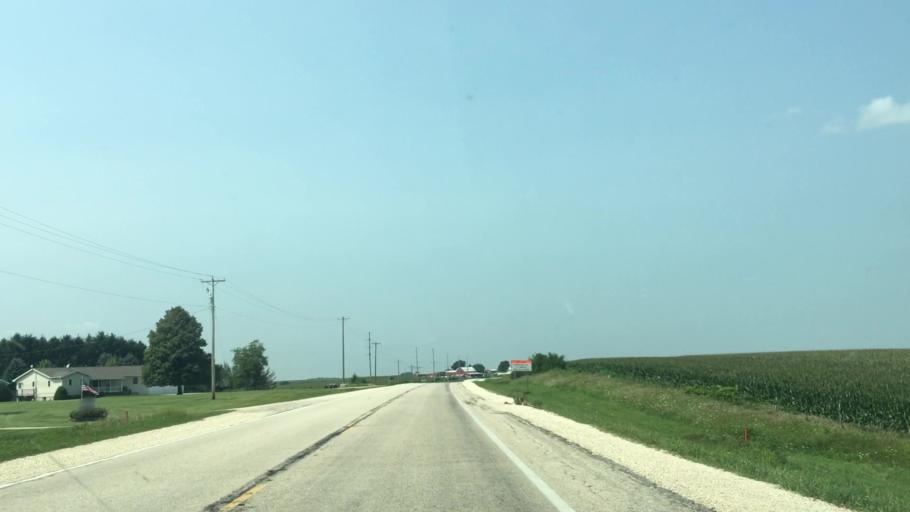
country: US
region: Iowa
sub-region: Fayette County
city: West Union
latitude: 42.9732
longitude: -91.8188
